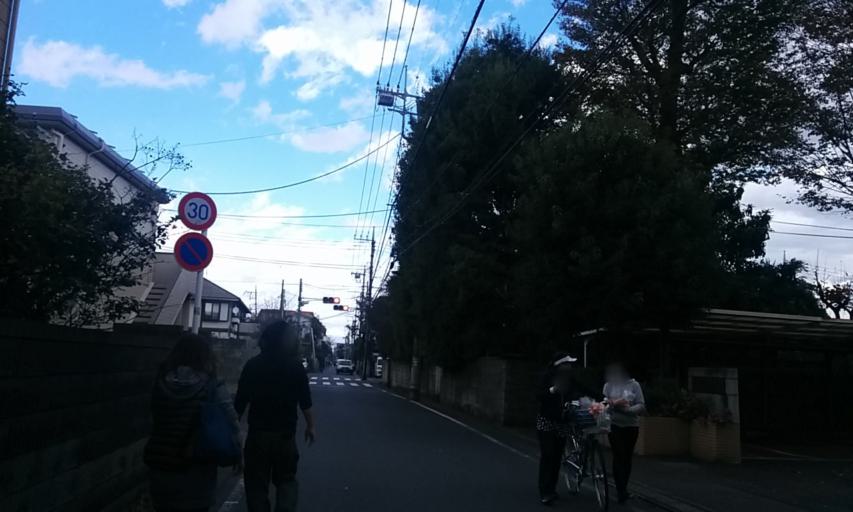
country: JP
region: Tokyo
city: Tokyo
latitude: 35.6742
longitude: 139.6377
